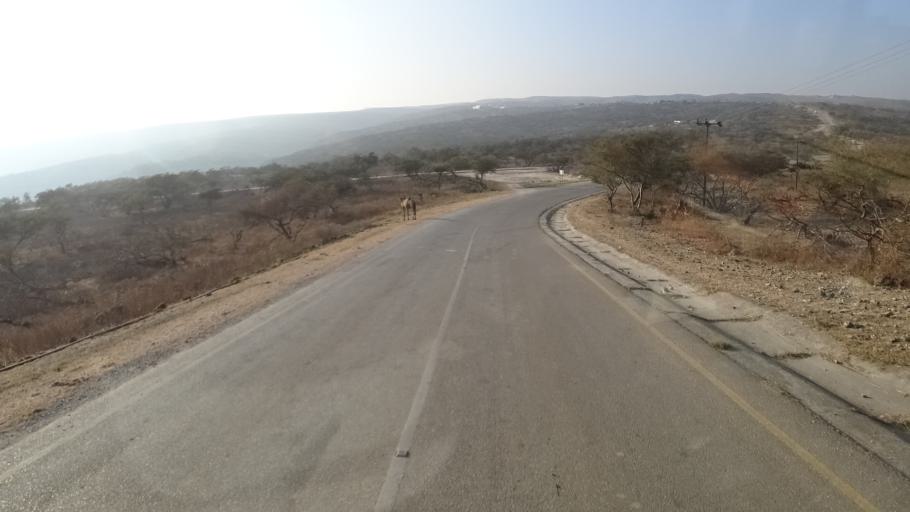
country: YE
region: Al Mahrah
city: Hawf
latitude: 16.7804
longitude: 53.3318
